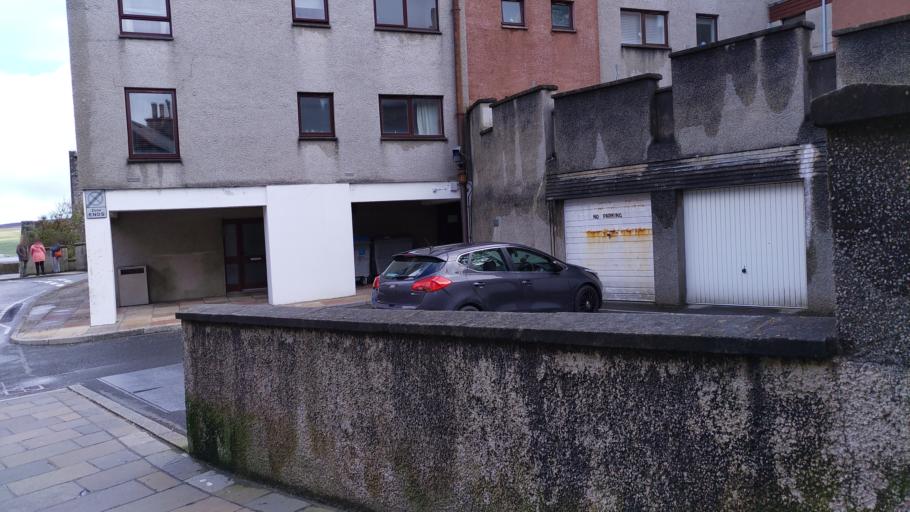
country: GB
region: Scotland
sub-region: Shetland Islands
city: Shetland
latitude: 60.1526
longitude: -1.1378
